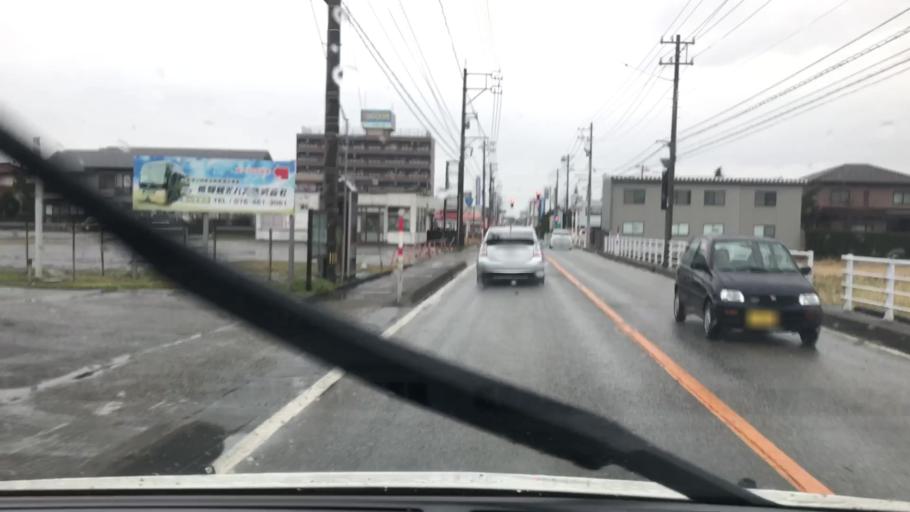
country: JP
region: Toyama
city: Yatsuomachi-higashikumisaka
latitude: 36.5882
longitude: 137.2054
